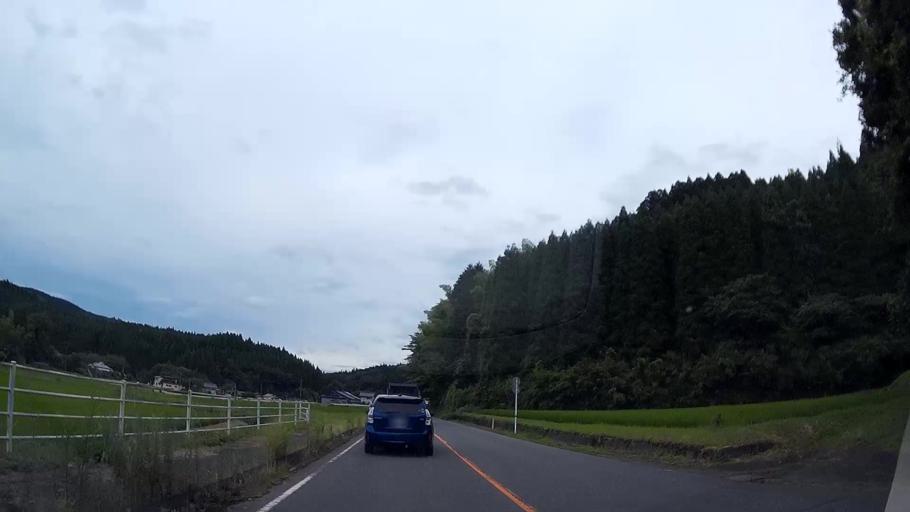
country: JP
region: Oita
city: Tsukawaki
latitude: 33.1262
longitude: 131.0328
